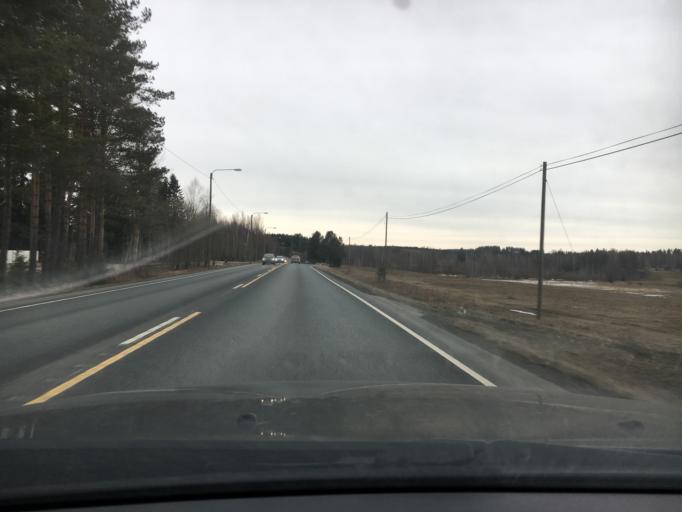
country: FI
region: Northern Savo
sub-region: Kuopio
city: Siilinjaervi
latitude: 63.1088
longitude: 27.6460
